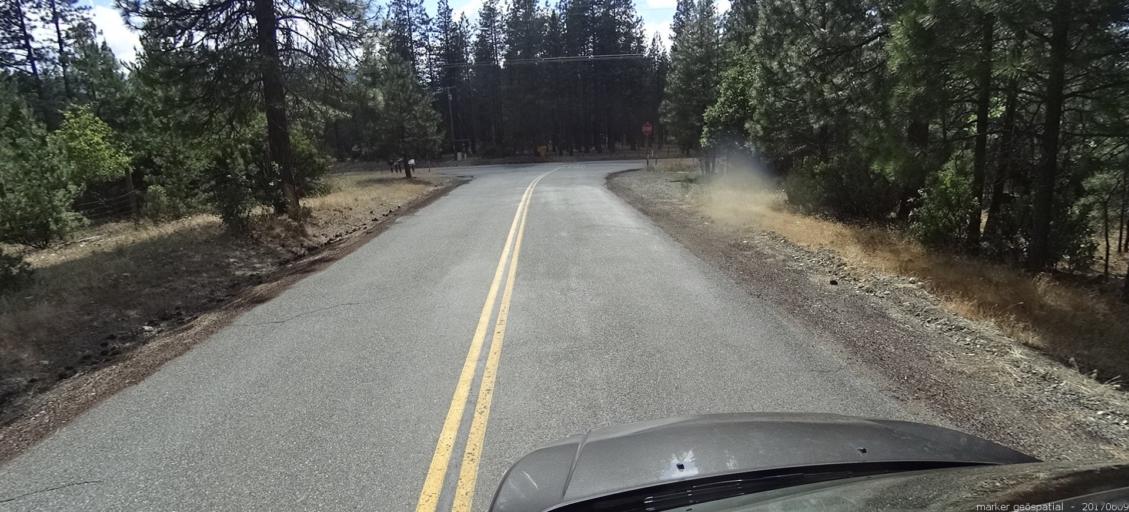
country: US
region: California
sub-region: Siskiyou County
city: Yreka
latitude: 41.5150
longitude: -122.9059
